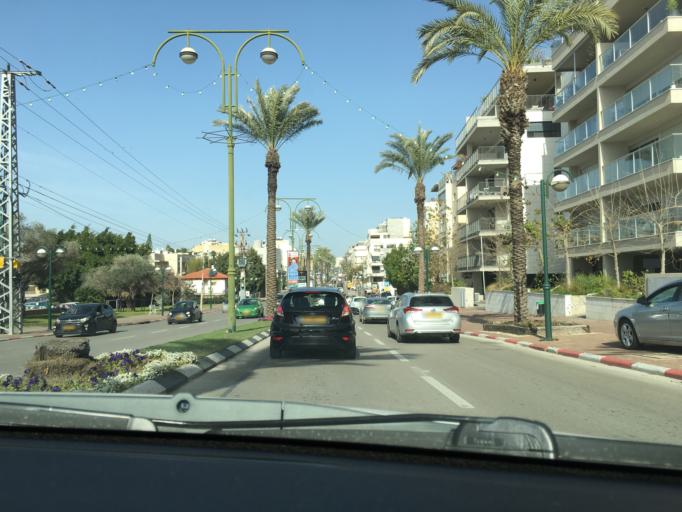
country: IL
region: Tel Aviv
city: Ramat HaSharon
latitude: 32.1392
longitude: 34.8358
